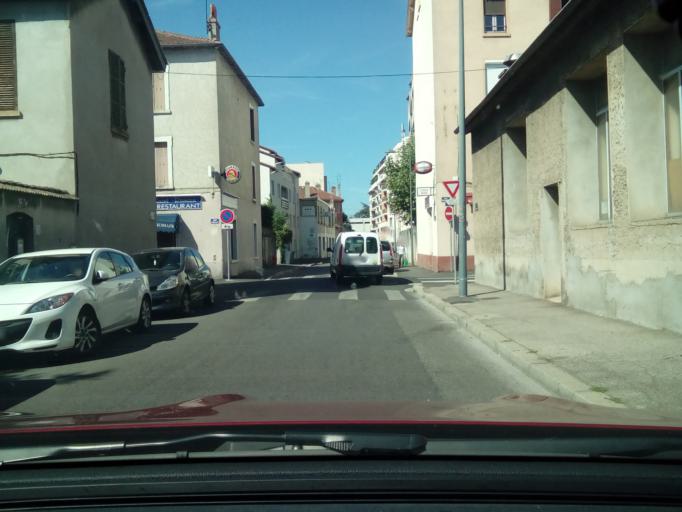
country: FR
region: Rhone-Alpes
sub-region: Departement du Rhone
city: Villeurbanne
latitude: 45.7582
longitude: 4.8938
